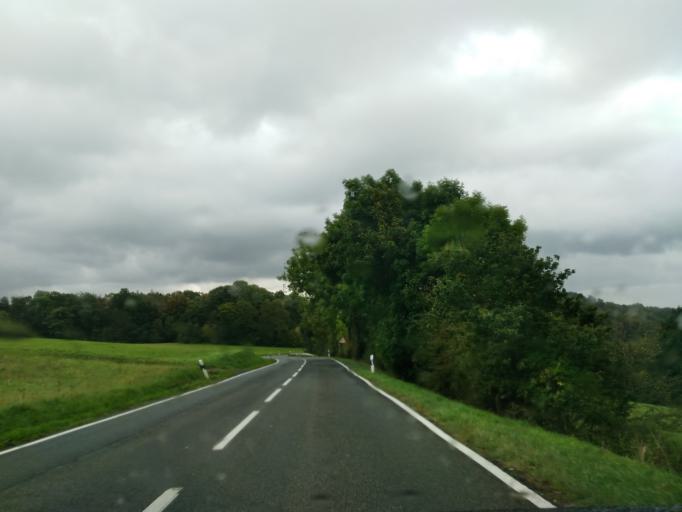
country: DE
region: Rheinland-Pfalz
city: Asbach
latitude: 50.6673
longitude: 7.3839
